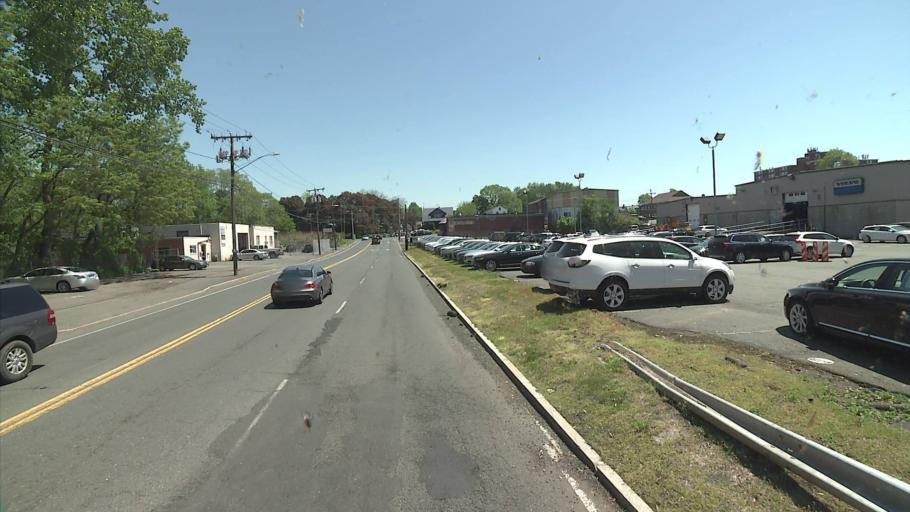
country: US
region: Connecticut
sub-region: Hartford County
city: Hartford
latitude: 41.7710
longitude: -72.6512
